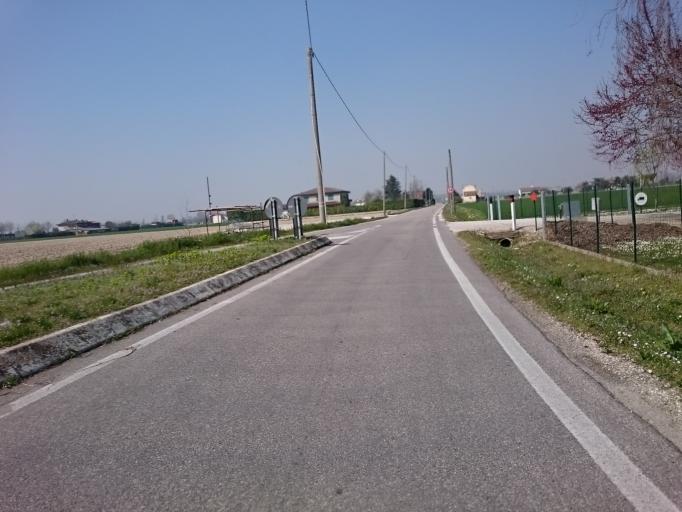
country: IT
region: Veneto
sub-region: Provincia di Padova
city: Villa Estense
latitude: 45.1834
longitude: 11.6721
